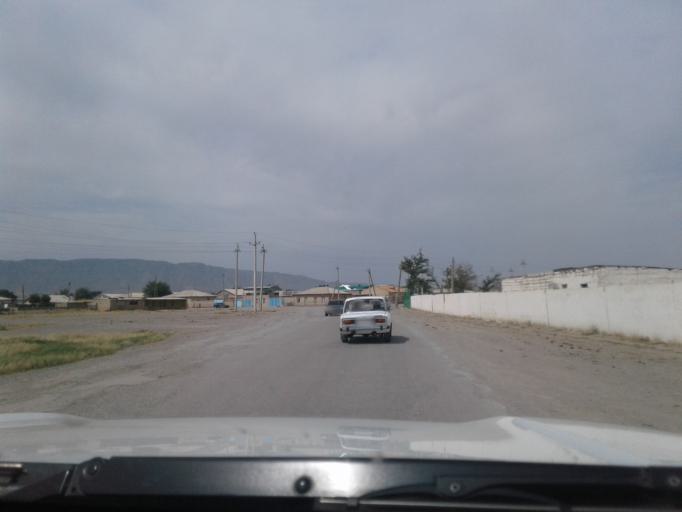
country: TM
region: Balkan
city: Serdar
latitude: 38.9913
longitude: 56.2696
